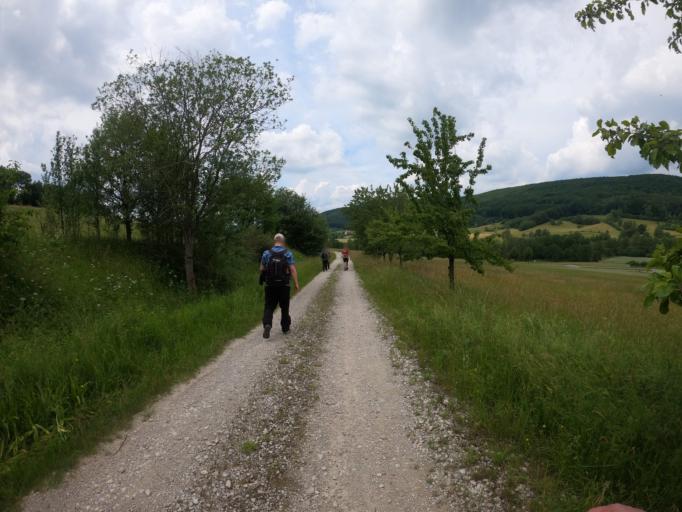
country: DE
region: Bavaria
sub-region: Upper Franconia
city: Litzendorf
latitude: 49.9157
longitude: 11.0597
